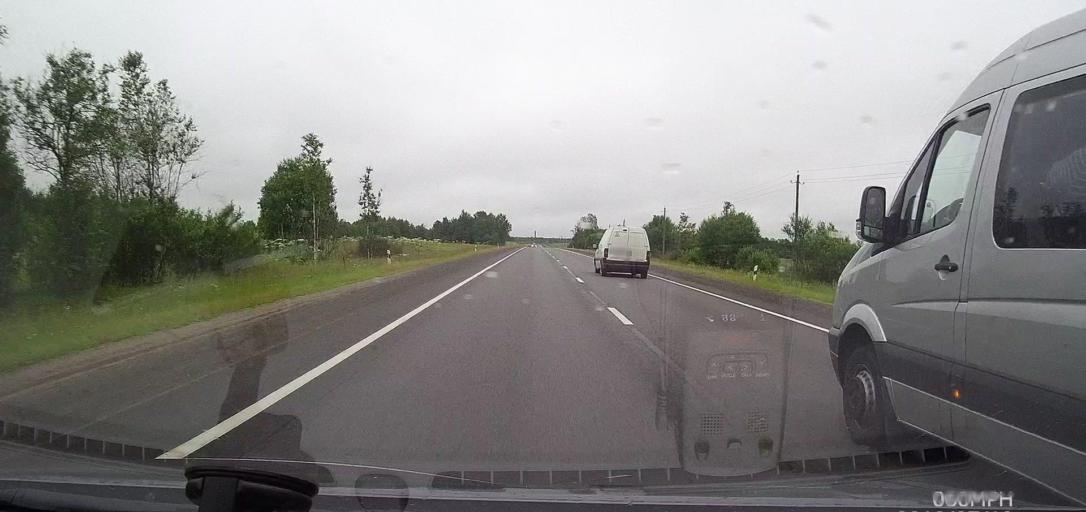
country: RU
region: Leningrad
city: Staraya Ladoga
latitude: 59.9914
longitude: 32.0833
